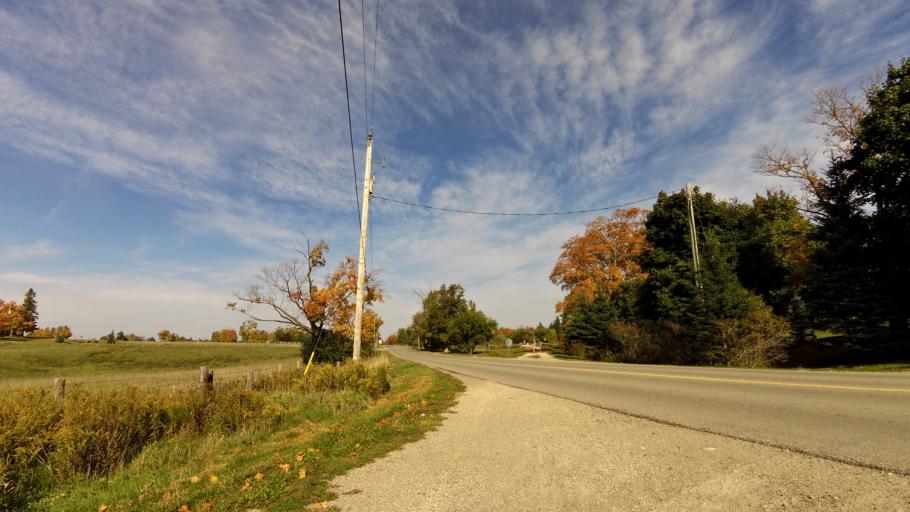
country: CA
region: Ontario
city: Orangeville
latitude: 43.7814
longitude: -80.0630
